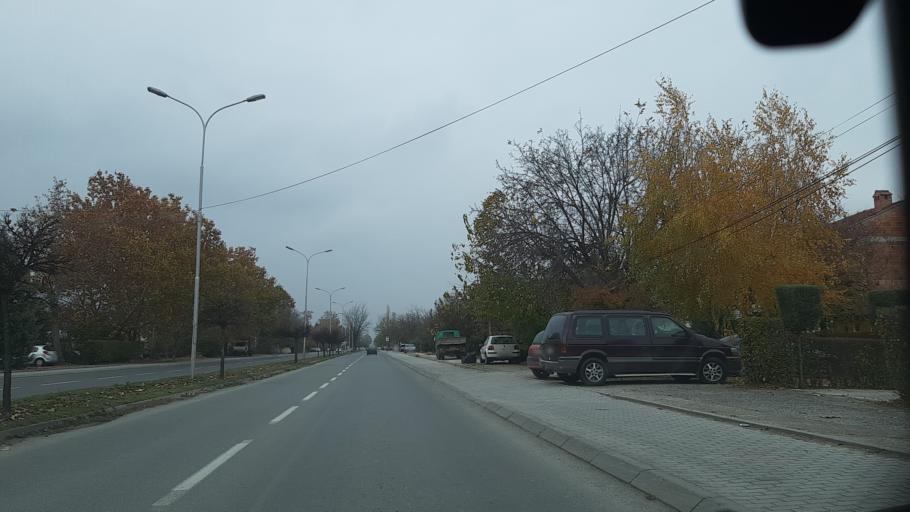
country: MK
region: Kisela Voda
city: Usje
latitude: 41.9720
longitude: 21.4761
